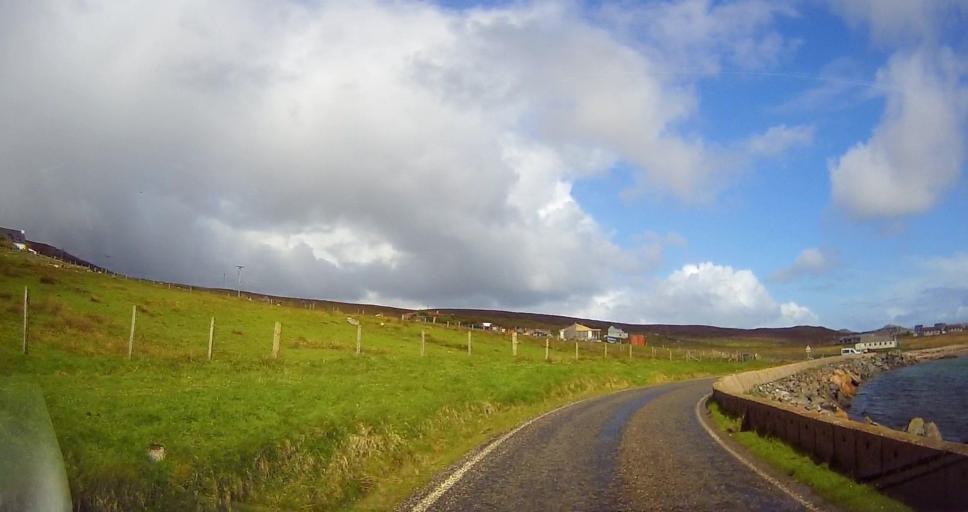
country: GB
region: Scotland
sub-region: Shetland Islands
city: Lerwick
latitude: 60.5821
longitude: -1.3350
